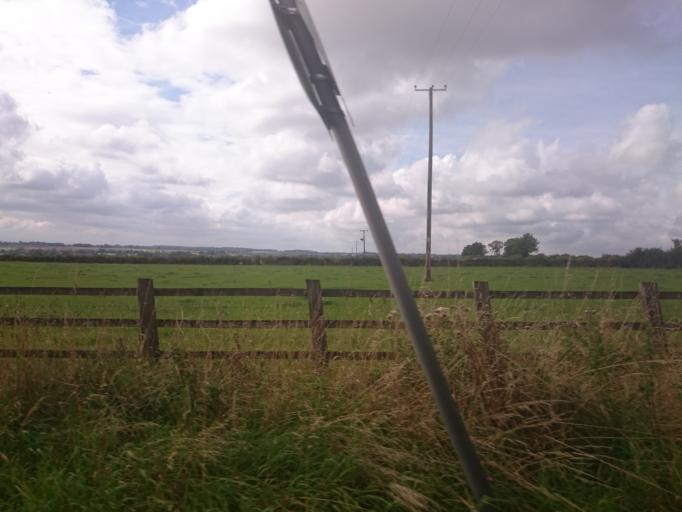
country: GB
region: England
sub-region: Gloucestershire
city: Coates
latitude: 51.7853
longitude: -2.0404
